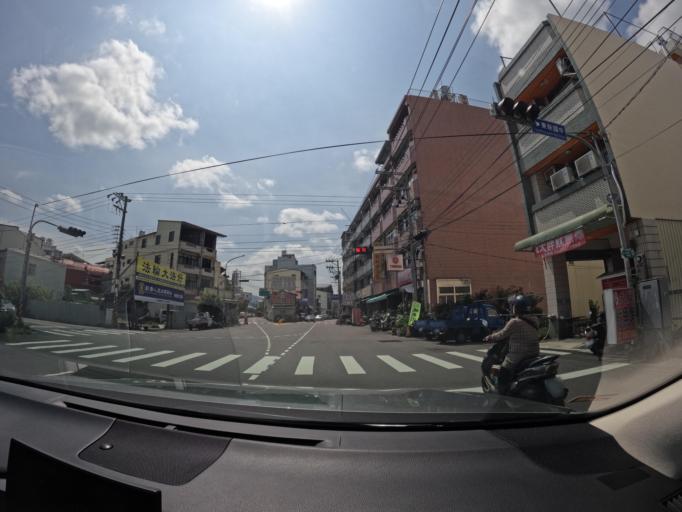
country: TW
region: Taiwan
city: Fengyuan
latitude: 24.2622
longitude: 120.8267
